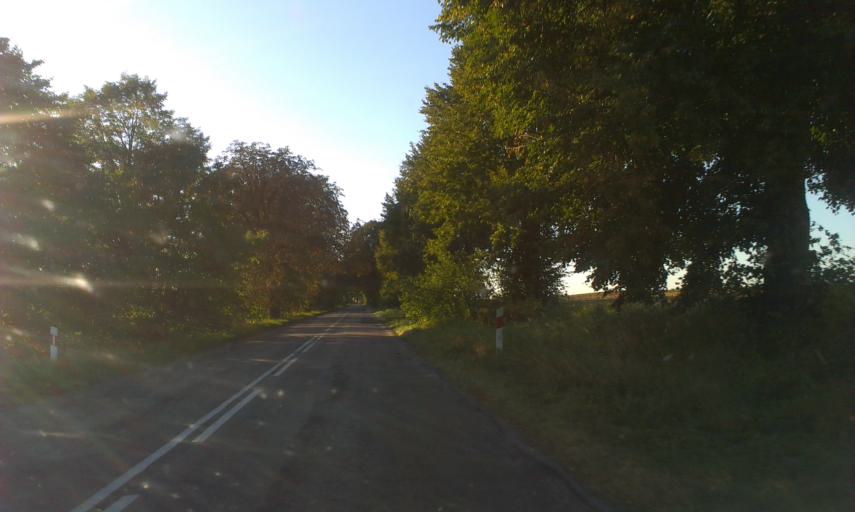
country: PL
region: Pomeranian Voivodeship
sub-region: Powiat czluchowski
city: Rzeczenica
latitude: 53.6404
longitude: 17.1553
